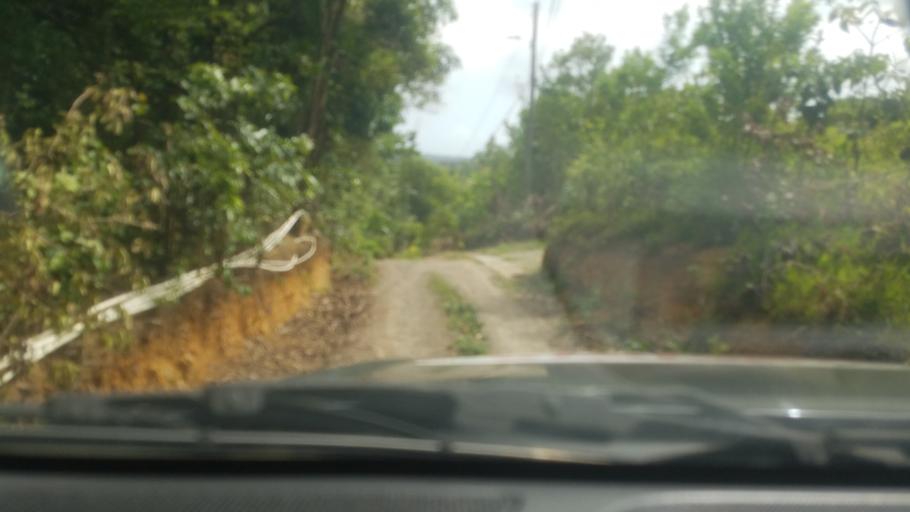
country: LC
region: Micoud Quarter
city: Micoud
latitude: 13.7942
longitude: -60.9263
